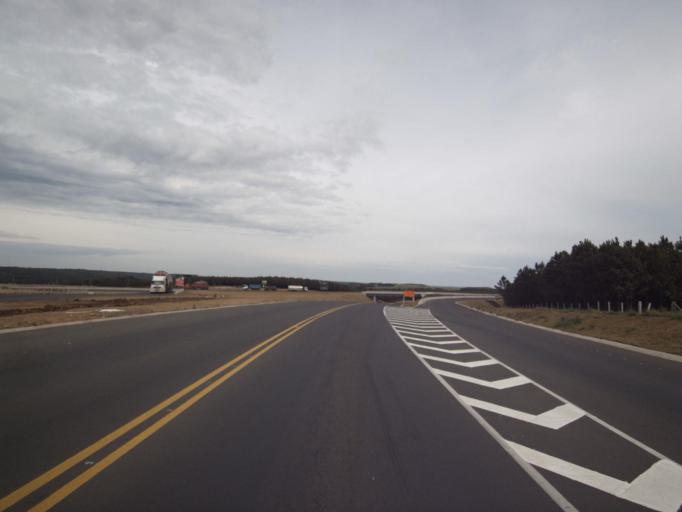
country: BR
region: Santa Catarina
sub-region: Cacador
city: Cacador
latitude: -26.6071
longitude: -51.4800
